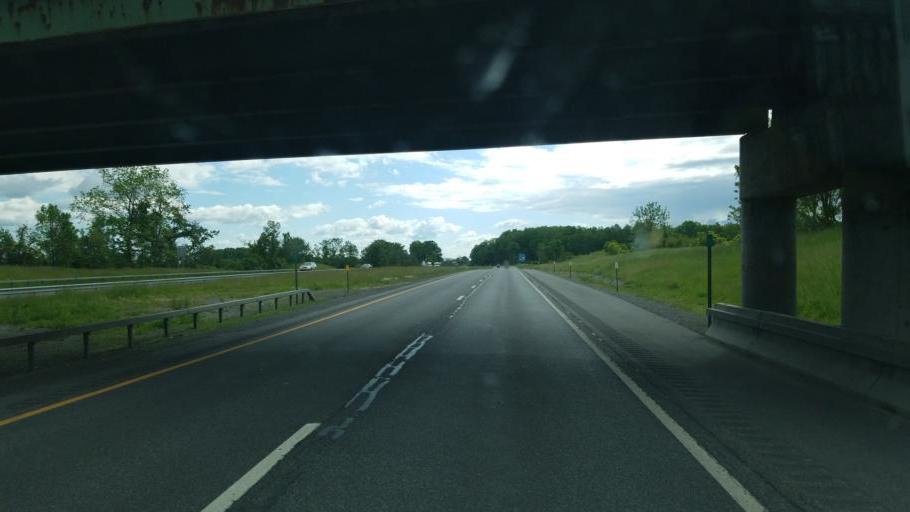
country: US
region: New York
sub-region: Seneca County
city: Seneca Falls
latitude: 42.9721
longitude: -76.8170
